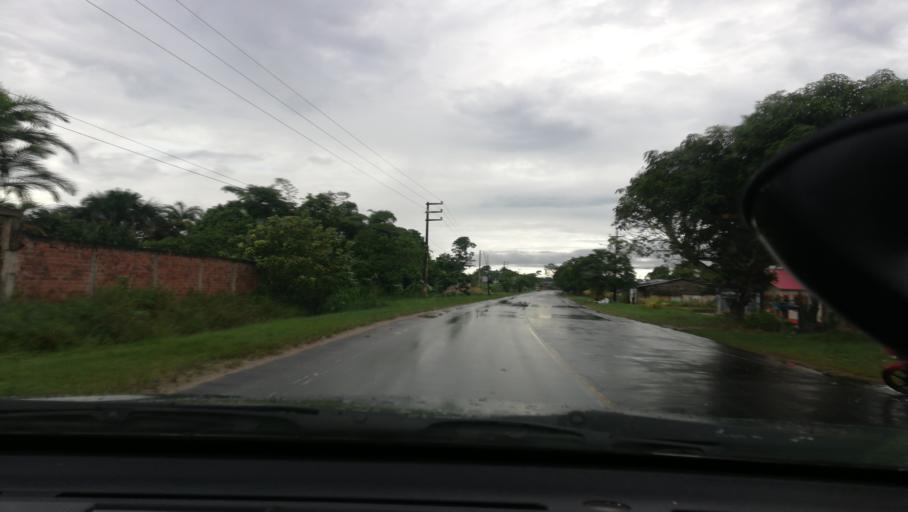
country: PE
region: Loreto
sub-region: Provincia de Maynas
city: Iquitos
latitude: -3.8609
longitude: -73.3370
